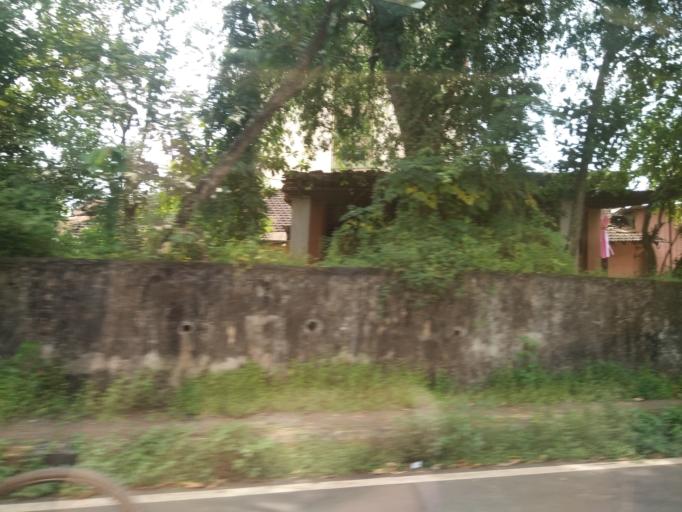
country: IN
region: Goa
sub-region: South Goa
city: Madgaon
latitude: 15.2612
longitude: 73.9636
